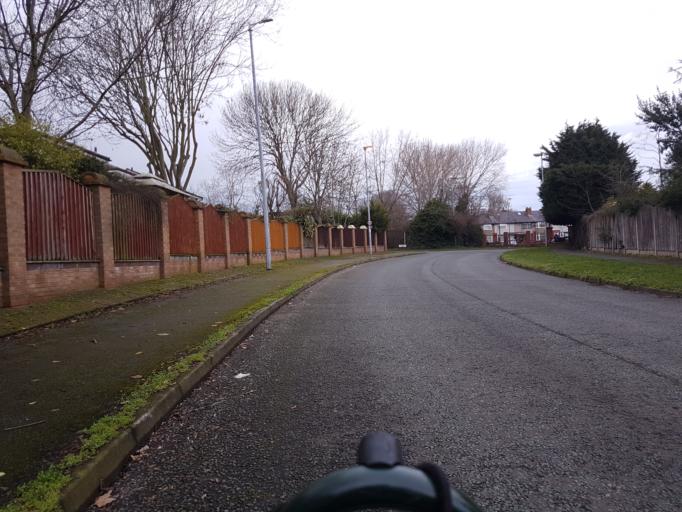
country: GB
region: England
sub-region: Metropolitan Borough of Wirral
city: Bromborough
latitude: 53.3768
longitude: -2.9613
